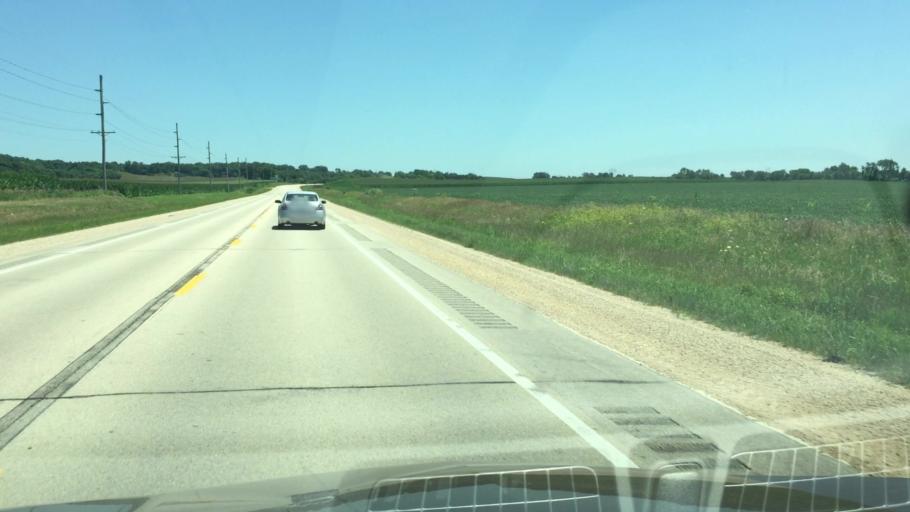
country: US
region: Iowa
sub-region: Jackson County
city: Maquoketa
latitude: 42.0659
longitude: -90.7735
